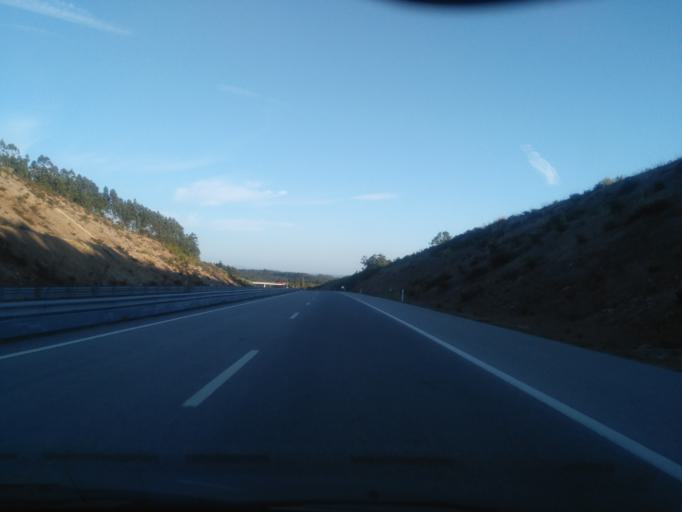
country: PT
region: Coimbra
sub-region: Figueira da Foz
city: Alhadas
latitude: 40.1862
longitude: -8.8103
